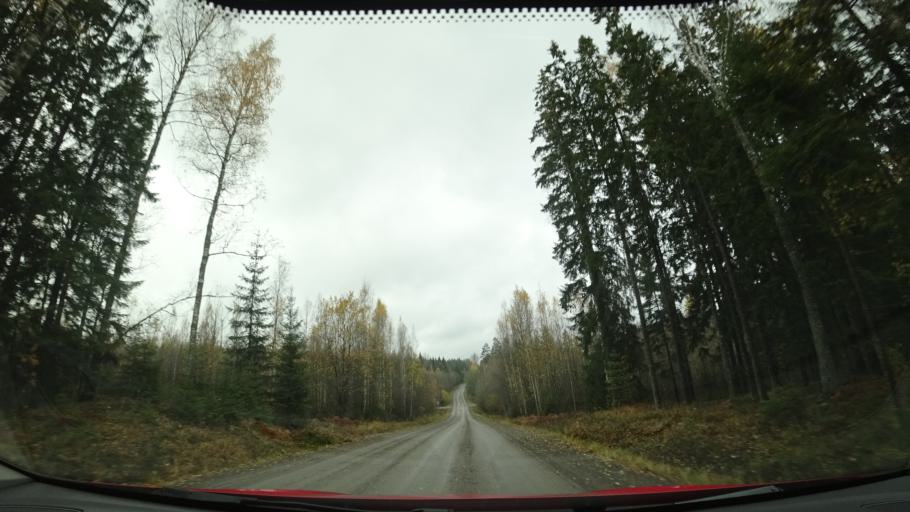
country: FI
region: Uusimaa
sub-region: Helsinki
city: Sibbo
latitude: 60.3013
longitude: 25.1985
